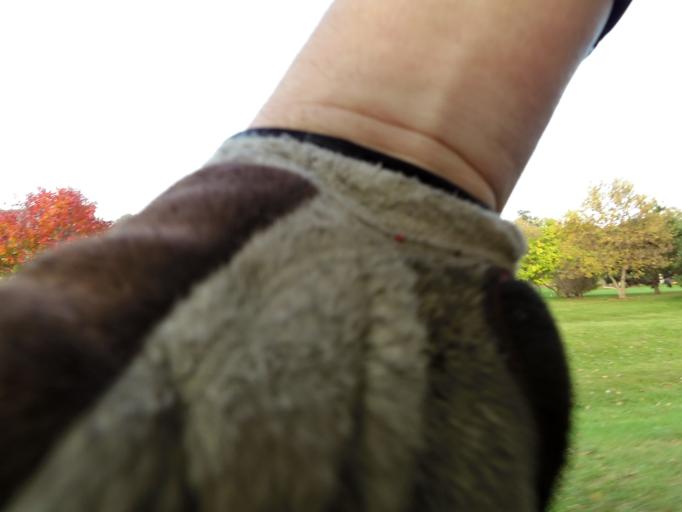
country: US
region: Minnesota
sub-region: Washington County
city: Lakeland
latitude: 44.9793
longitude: -92.8037
